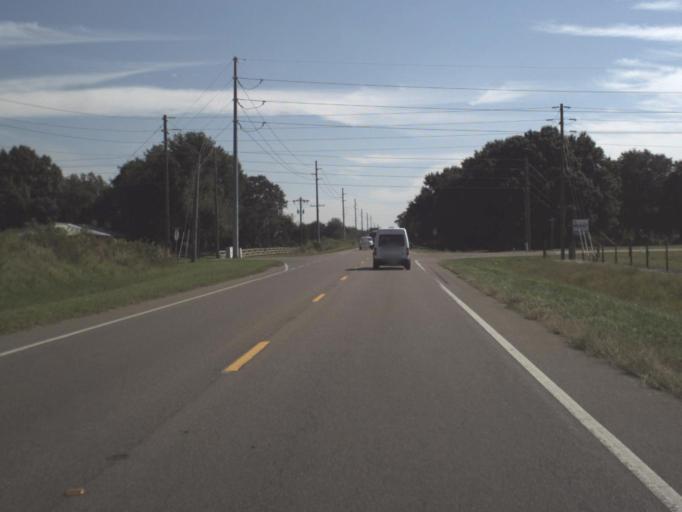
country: US
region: Florida
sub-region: Hardee County
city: Wauchula
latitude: 27.5514
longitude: -81.7693
